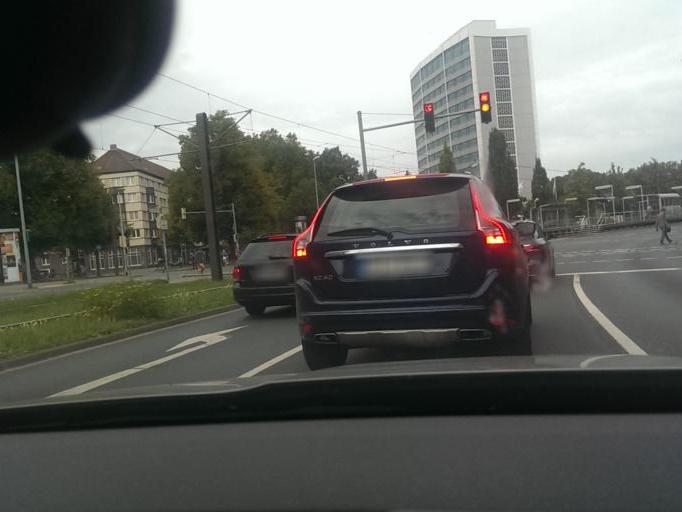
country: DE
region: Lower Saxony
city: Hannover
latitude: 52.3612
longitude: 9.7214
